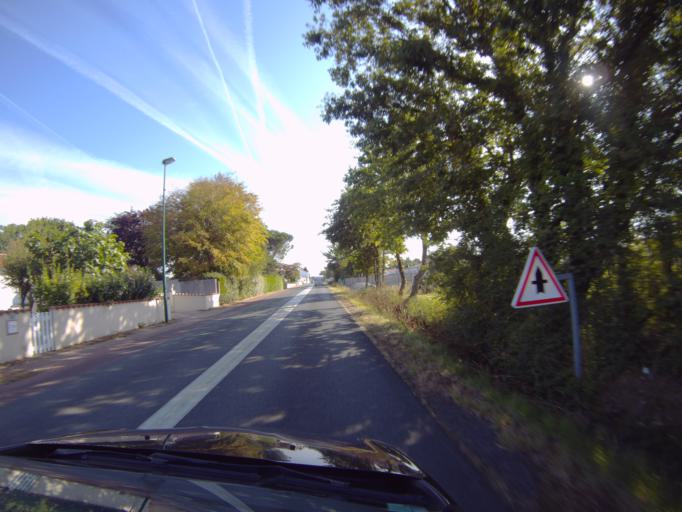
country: FR
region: Pays de la Loire
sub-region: Departement de la Vendee
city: Saint-Hilaire-de-Talmont
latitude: 46.5043
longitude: -1.5736
